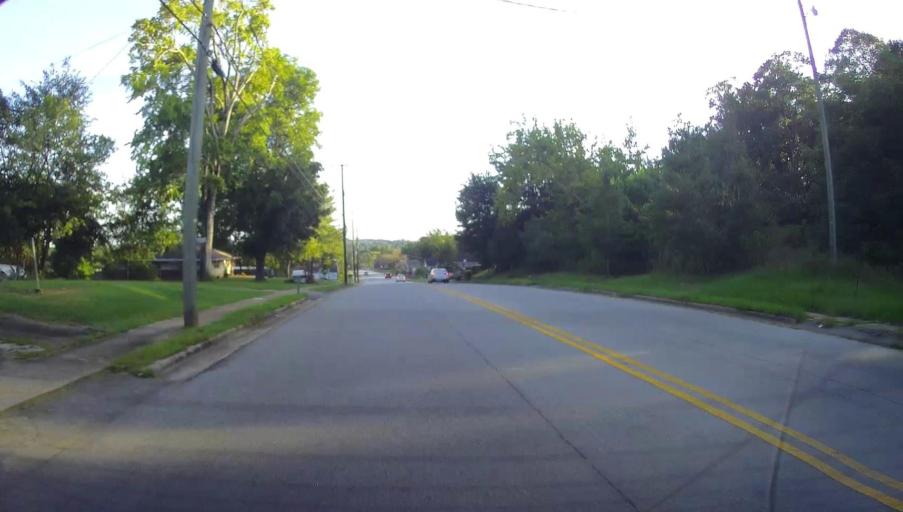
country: US
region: Georgia
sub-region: Muscogee County
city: Columbus
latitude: 32.4459
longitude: -85.0094
